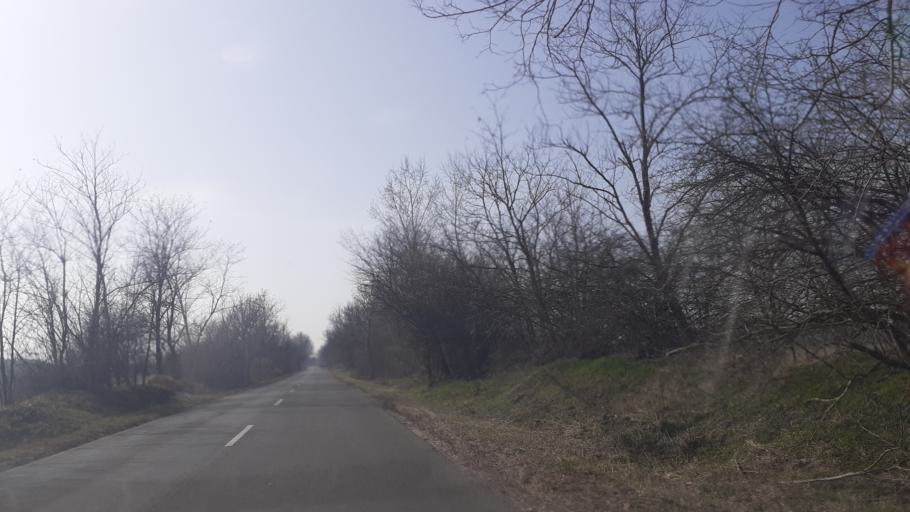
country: HU
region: Pest
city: Orkeny
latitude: 47.0899
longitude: 19.3807
